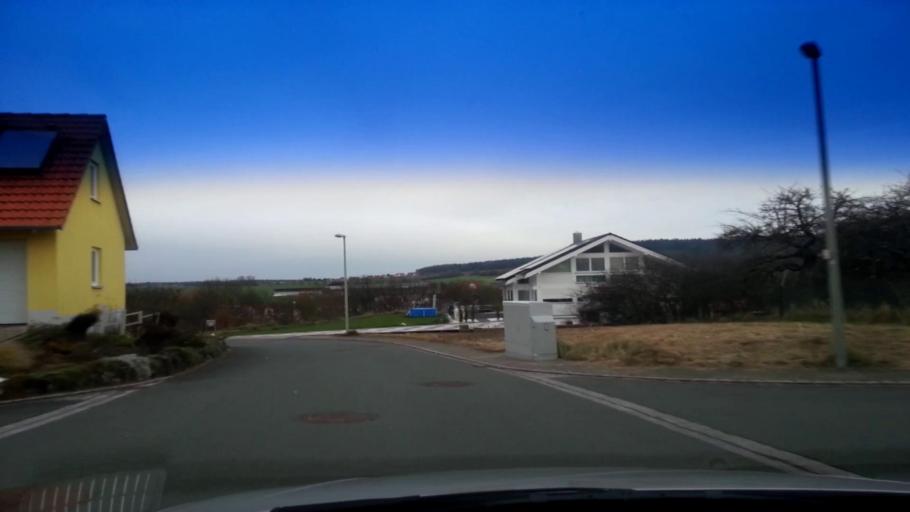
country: DE
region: Bavaria
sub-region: Upper Franconia
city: Litzendorf
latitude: 49.9100
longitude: 11.0174
